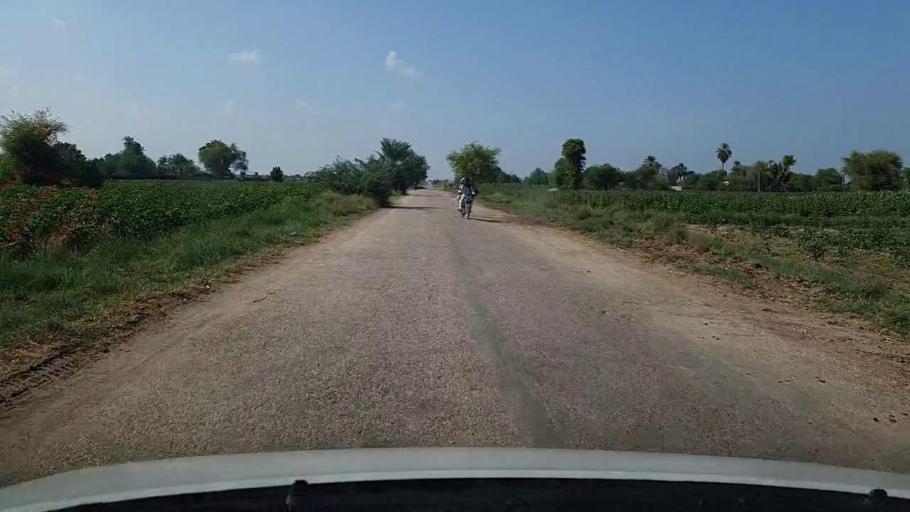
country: PK
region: Sindh
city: Kandiaro
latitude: 27.0581
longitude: 68.3168
